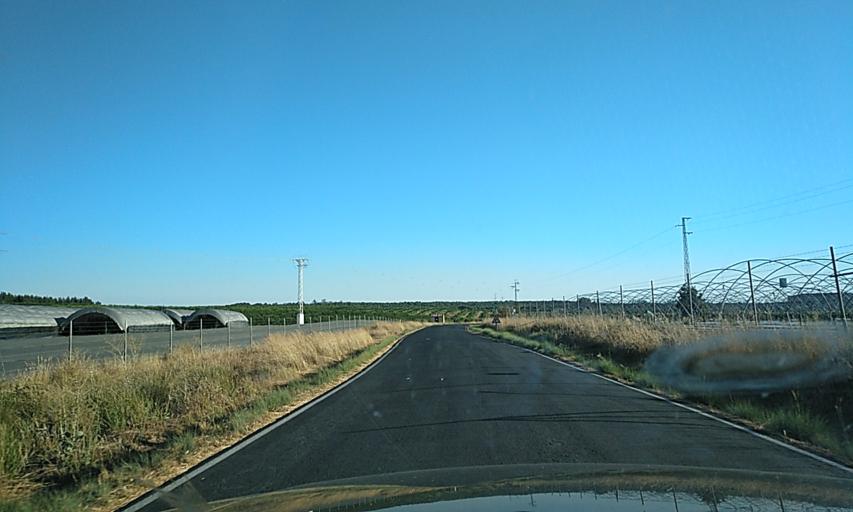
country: ES
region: Andalusia
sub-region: Provincia de Huelva
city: San Bartolome de la Torre
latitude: 37.4148
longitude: -7.1134
